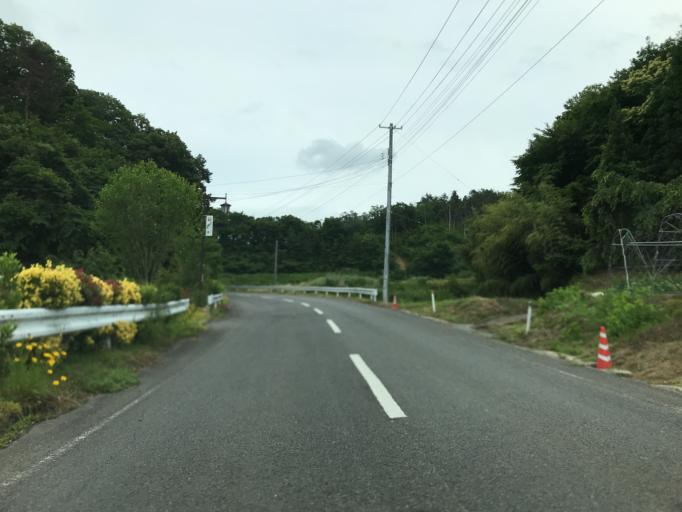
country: JP
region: Fukushima
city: Funehikimachi-funehiki
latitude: 37.3867
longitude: 140.5402
